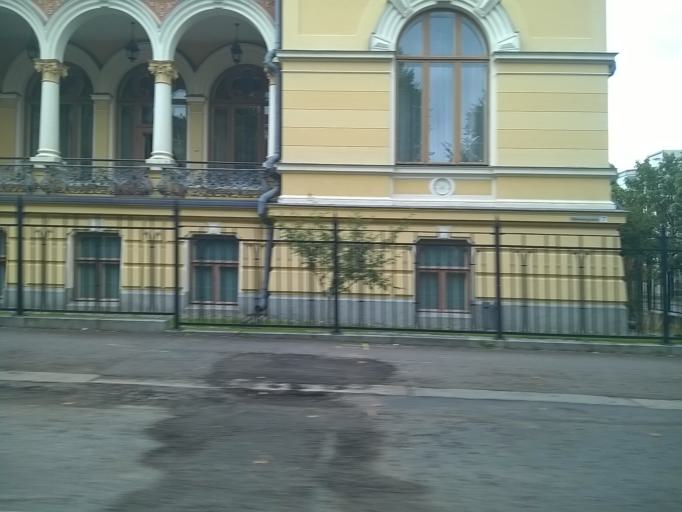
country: FI
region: Pirkanmaa
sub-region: Tampere
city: Tampere
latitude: 61.5016
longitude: 23.7510
